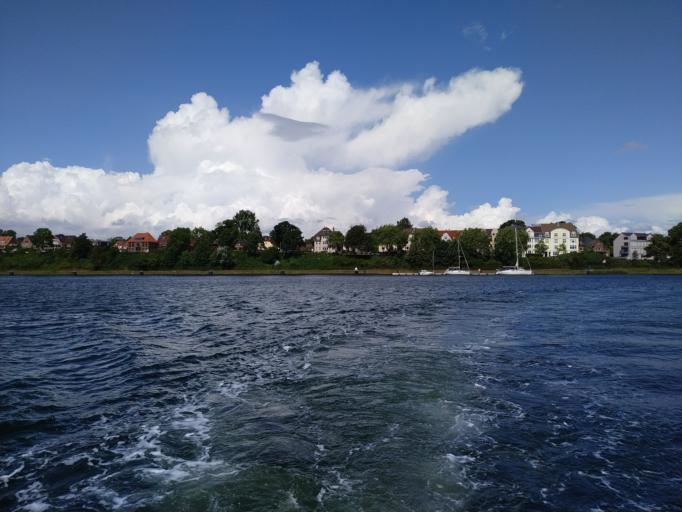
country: DE
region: Schleswig-Holstein
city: Altenholz
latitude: 54.3667
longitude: 10.1316
